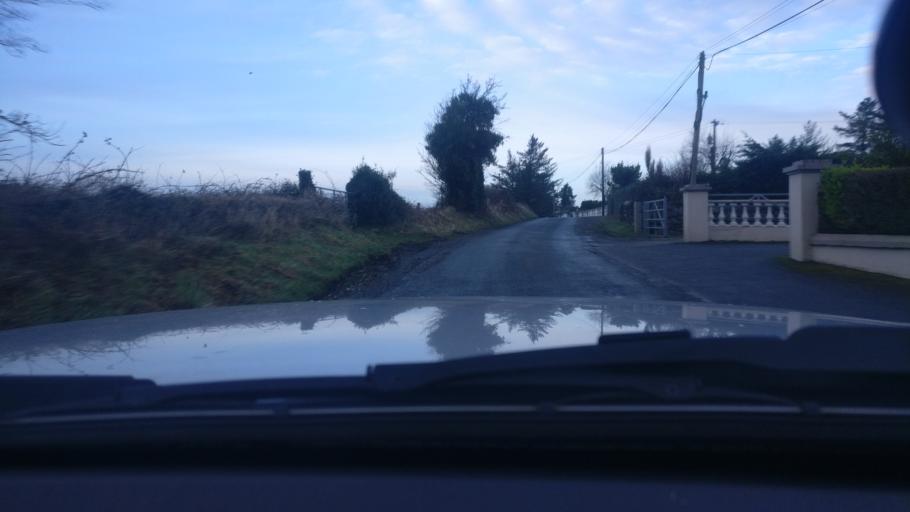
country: IE
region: Connaught
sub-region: County Galway
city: Loughrea
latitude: 53.1733
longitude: -8.5861
